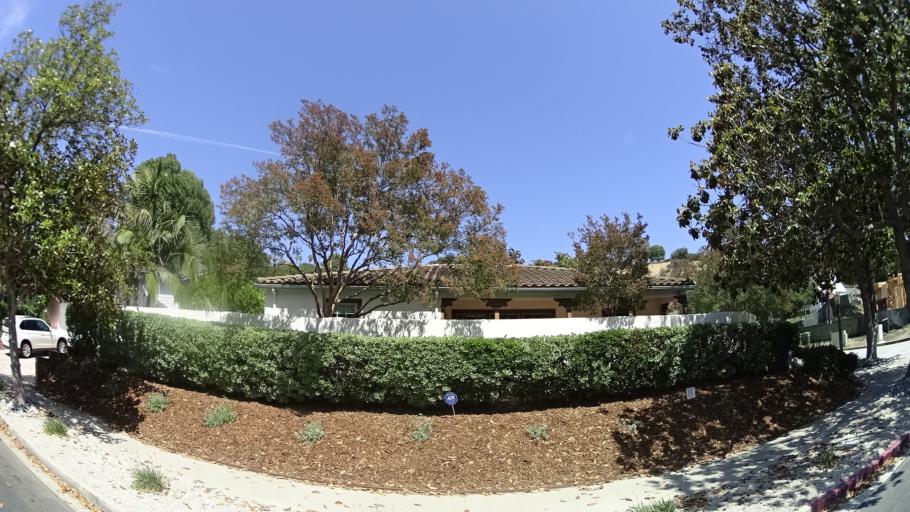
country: US
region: California
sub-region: Los Angeles County
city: Sherman Oaks
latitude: 34.1442
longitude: -118.4673
